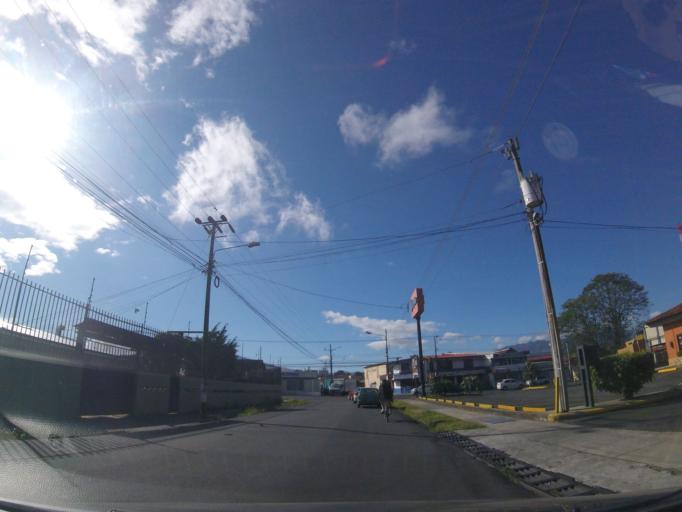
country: CR
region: San Jose
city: Calle Blancos
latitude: 9.9624
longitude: -84.0656
